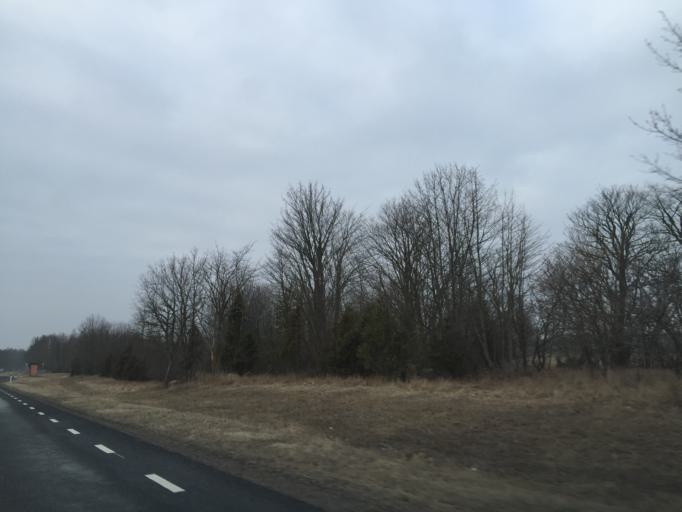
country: EE
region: Saare
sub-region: Orissaare vald
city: Orissaare
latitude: 58.5911
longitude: 23.3348
